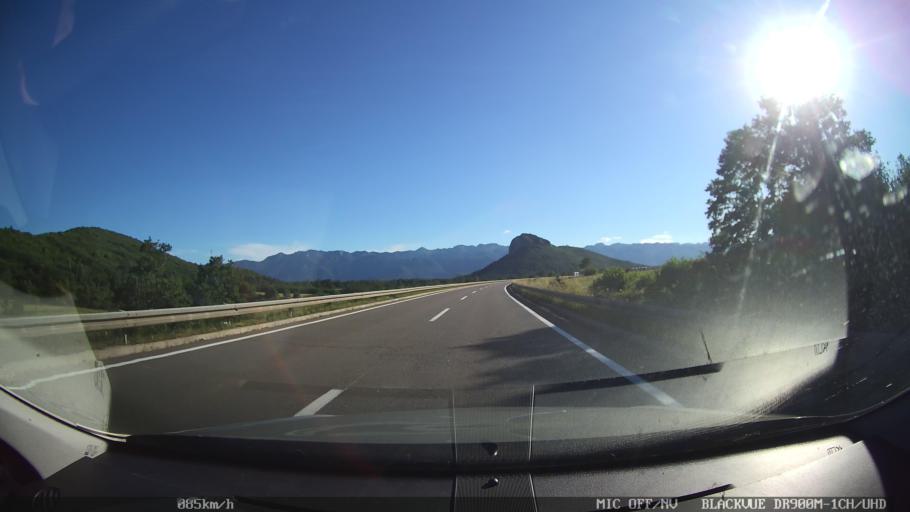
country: HR
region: Zadarska
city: Obrovac
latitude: 44.4421
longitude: 15.6393
